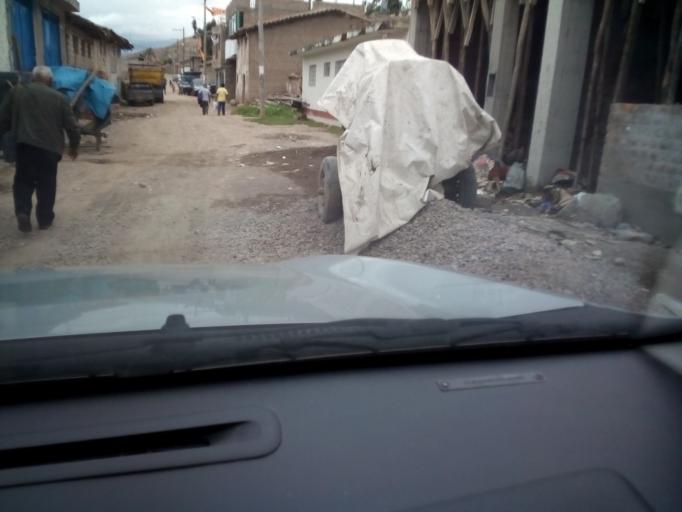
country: PE
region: Ayacucho
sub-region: Provincia de Huamanga
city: Ayacucho
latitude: -13.1660
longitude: -74.2490
